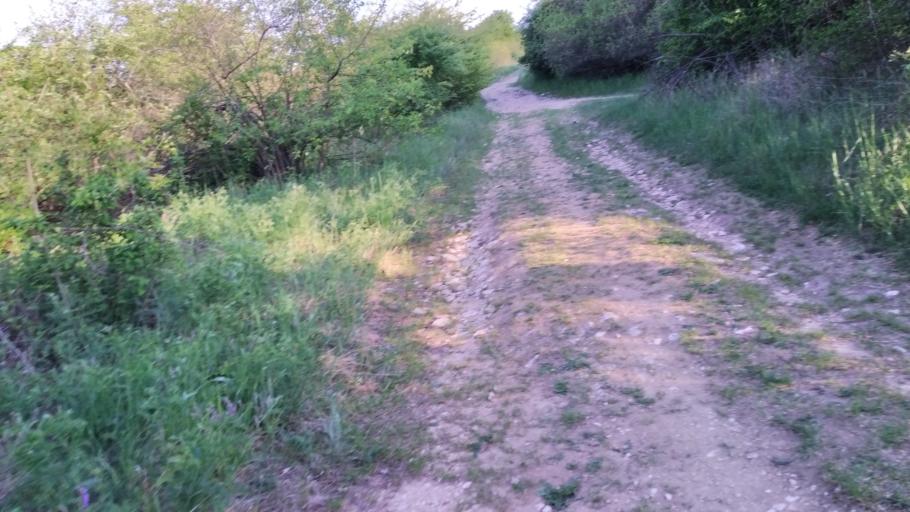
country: HU
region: Pest
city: Nagykovacsi
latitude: 47.6481
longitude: 18.9903
